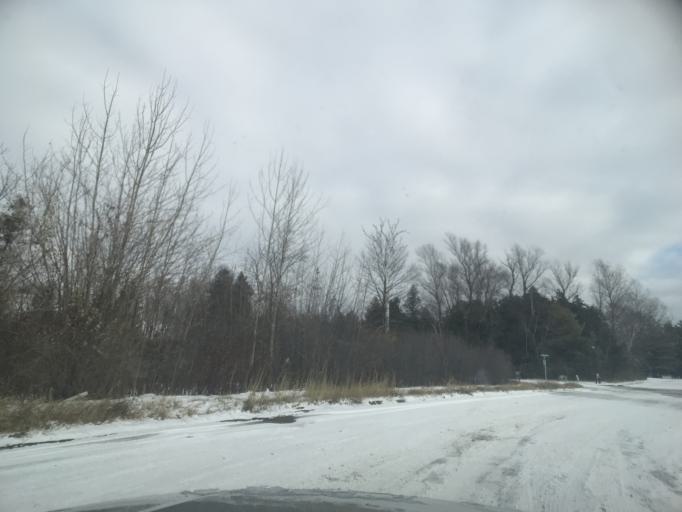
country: US
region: Wisconsin
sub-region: Door County
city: Sturgeon Bay
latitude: 44.8199
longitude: -87.3719
